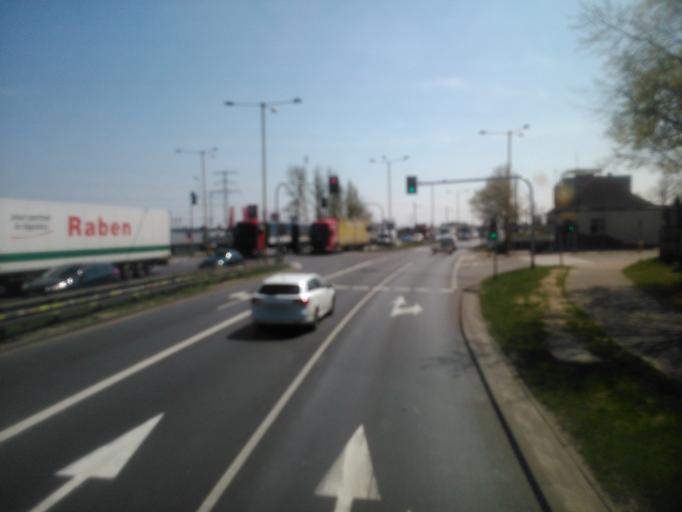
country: PL
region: Silesian Voivodeship
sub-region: Powiat czestochowski
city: Huta Stara B
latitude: 50.7675
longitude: 19.1639
